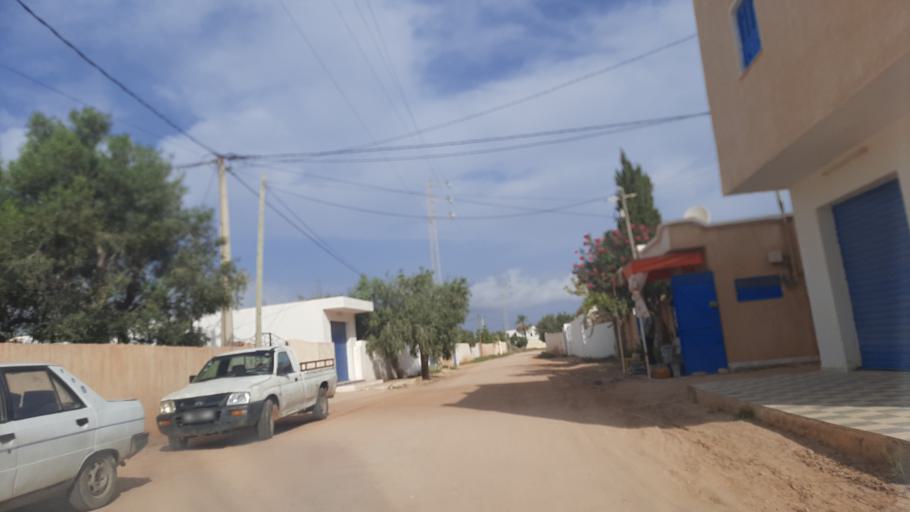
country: TN
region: Madanin
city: Midoun
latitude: 33.8138
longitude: 11.0252
